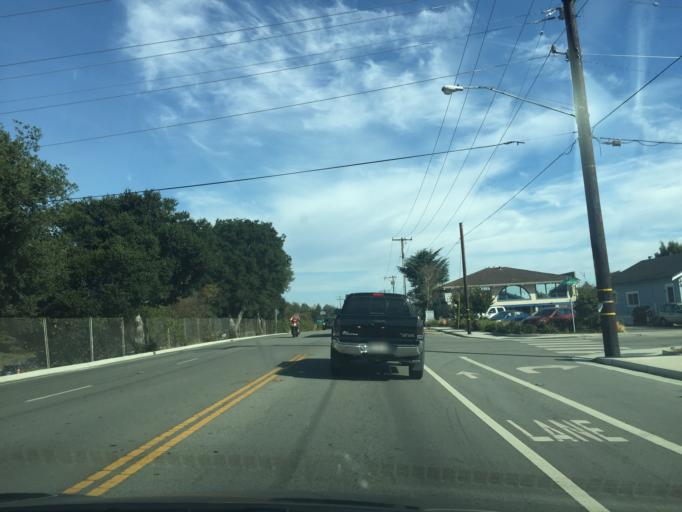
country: US
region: California
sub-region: Santa Cruz County
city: Live Oak
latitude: 36.9862
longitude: -121.9843
